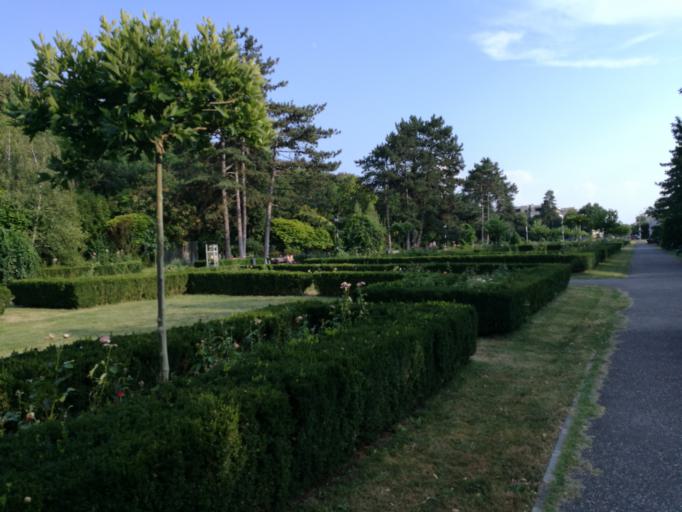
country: RO
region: Ilfov
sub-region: Comuna Otopeni
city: Otopeni
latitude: 44.5184
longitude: 26.0904
